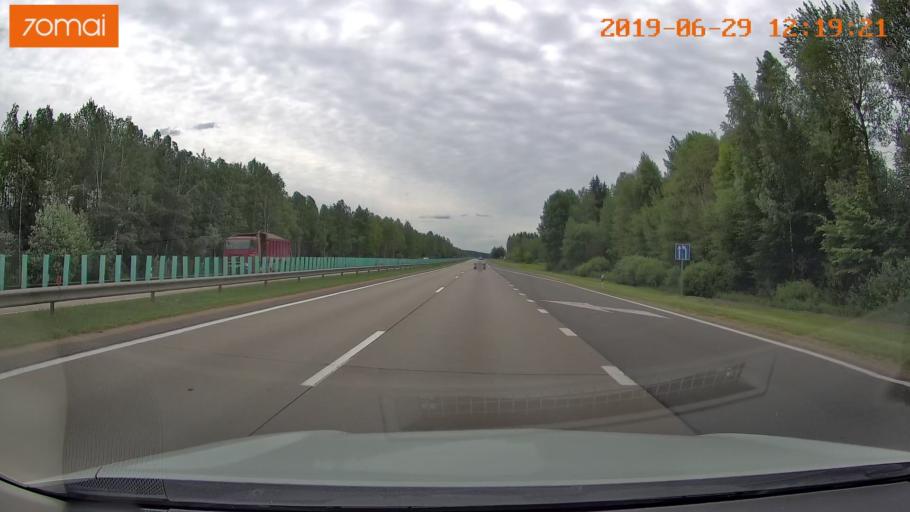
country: BY
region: Minsk
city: Samakhvalavichy
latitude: 53.5617
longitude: 27.4727
